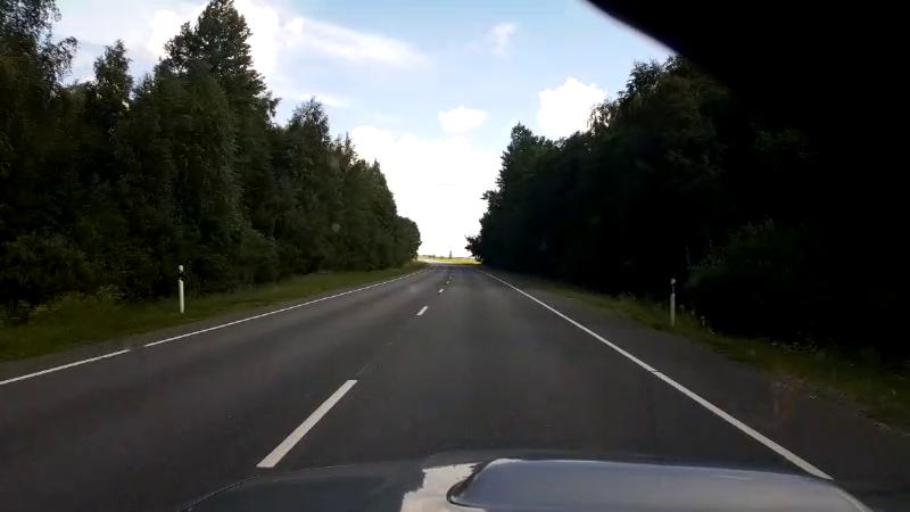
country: EE
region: Laeaene-Virumaa
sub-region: Tapa vald
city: Tapa
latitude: 59.2011
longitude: 25.8428
